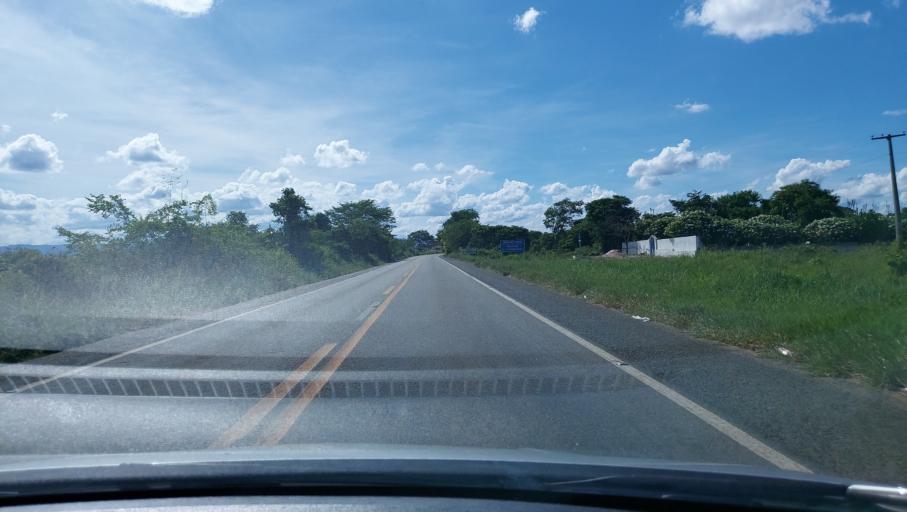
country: BR
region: Bahia
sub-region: Andarai
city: Vera Cruz
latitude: -12.5009
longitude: -41.2873
